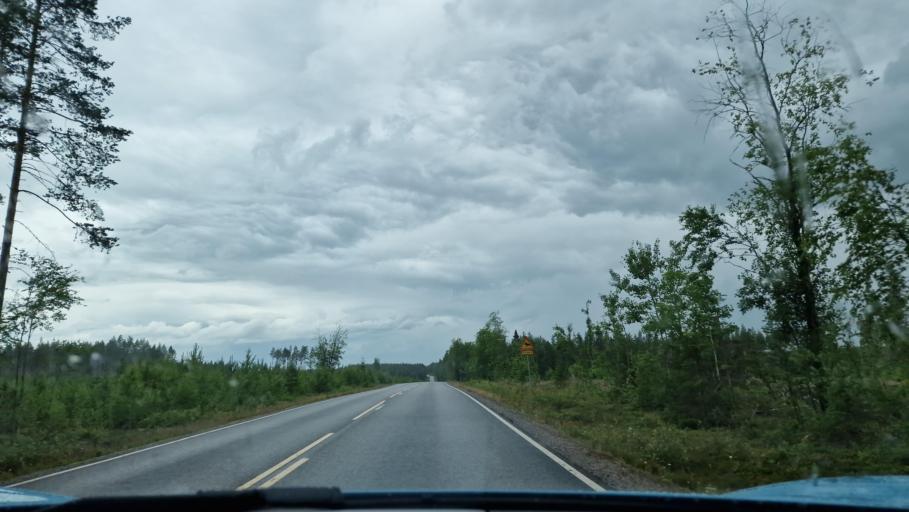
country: FI
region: Central Finland
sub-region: Saarijaervi-Viitasaari
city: Pylkoenmaeki
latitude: 62.6020
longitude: 24.5862
